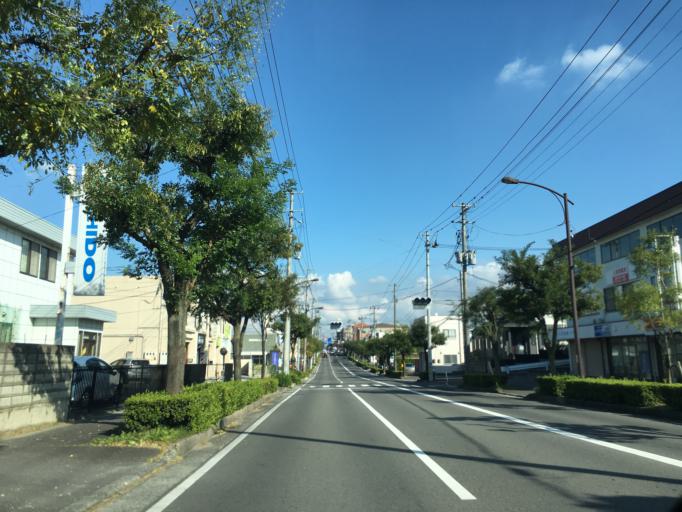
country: JP
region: Fukushima
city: Koriyama
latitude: 37.3861
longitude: 140.3522
